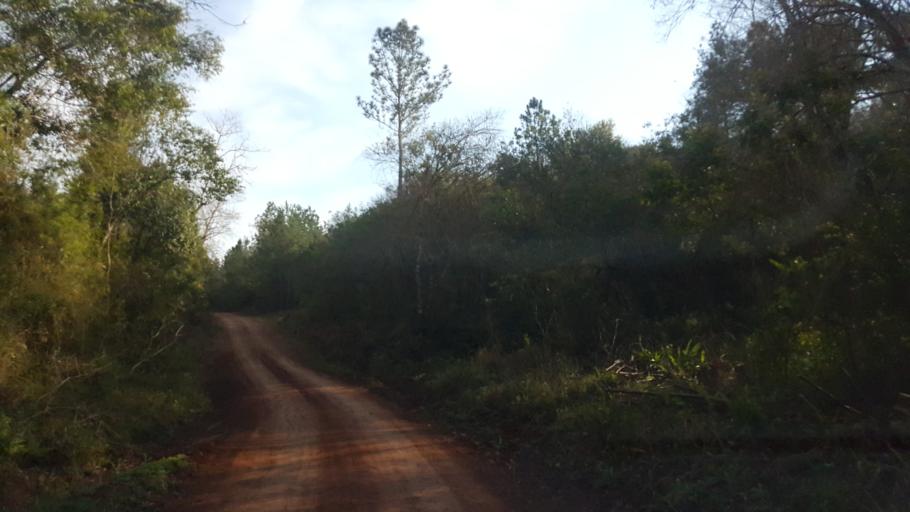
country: AR
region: Misiones
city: Capiovi
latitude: -26.9005
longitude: -55.0914
